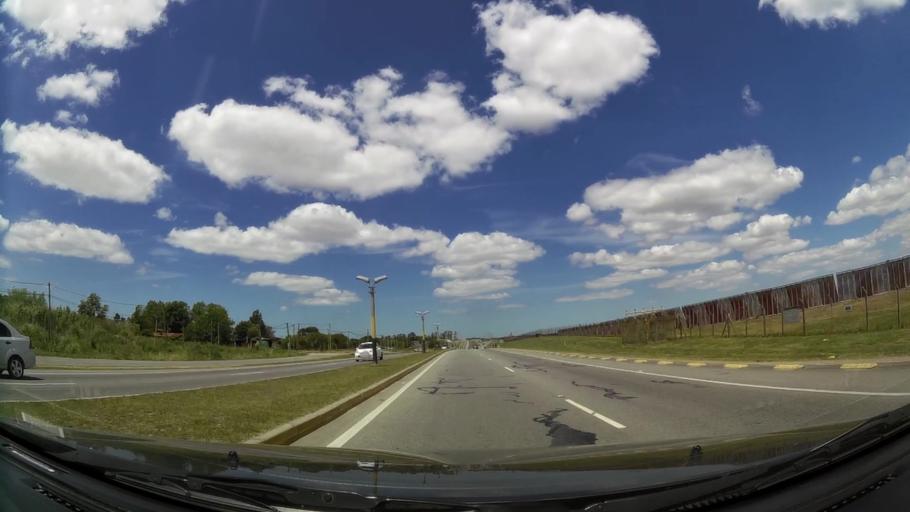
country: UY
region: Canelones
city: Colonia Nicolich
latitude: -34.8254
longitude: -56.0097
